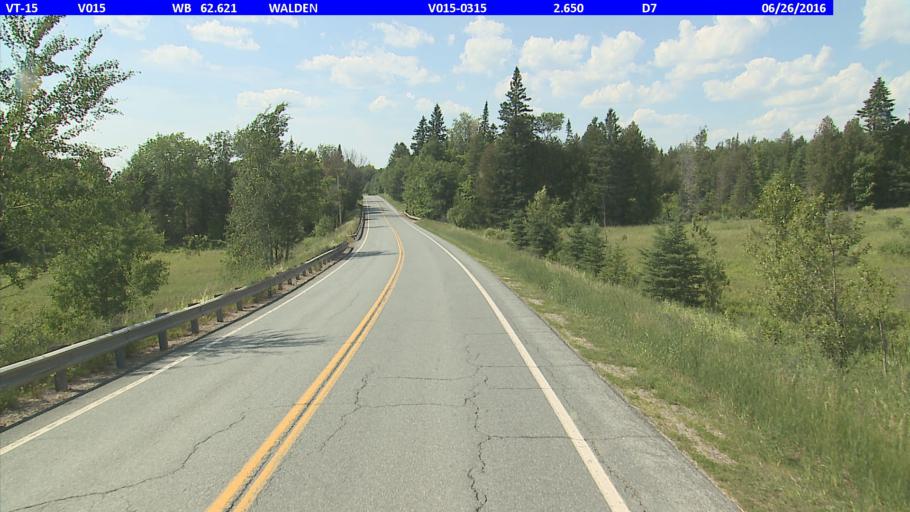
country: US
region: Vermont
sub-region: Caledonia County
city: Hardwick
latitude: 44.4619
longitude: -72.2648
